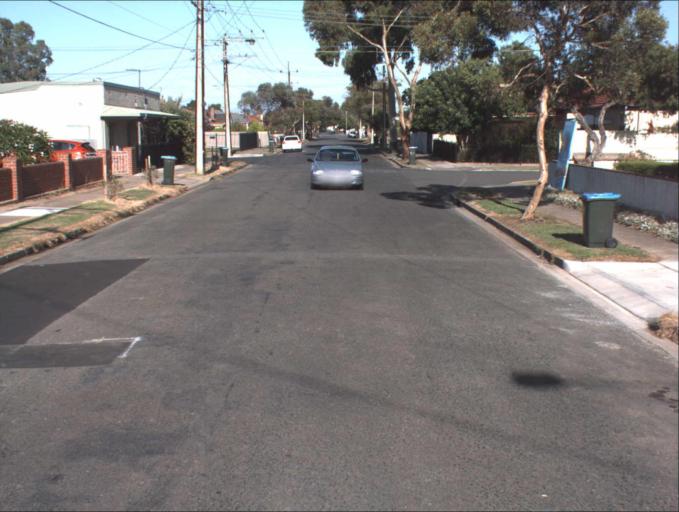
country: AU
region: South Australia
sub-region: Prospect
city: Prospect
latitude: -34.8841
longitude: 138.5744
